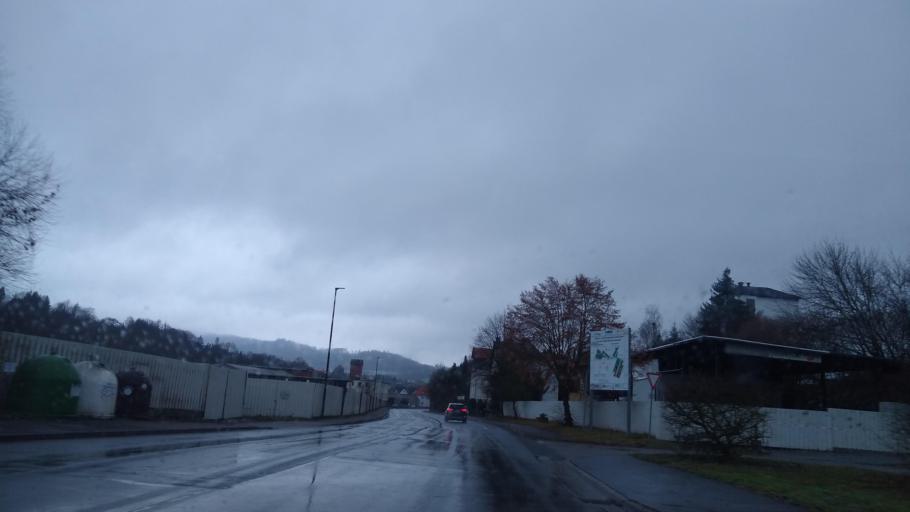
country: DE
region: Lower Saxony
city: Eschershausen
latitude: 51.9247
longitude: 9.6483
